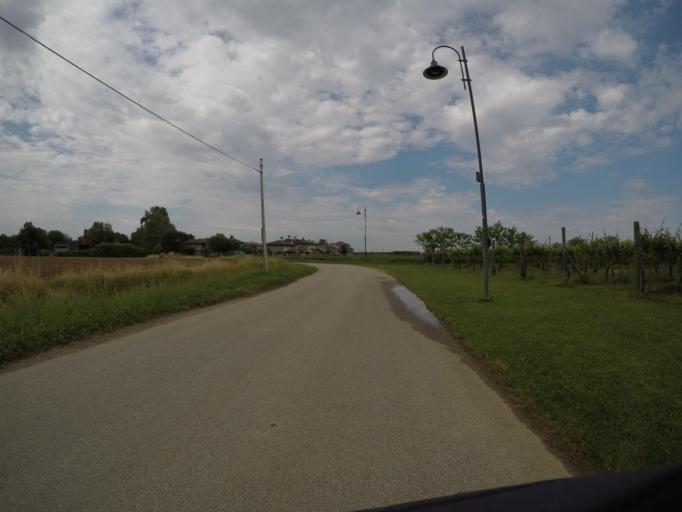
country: IT
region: Friuli Venezia Giulia
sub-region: Provincia di Udine
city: Percoto
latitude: 45.9627
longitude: 13.3102
